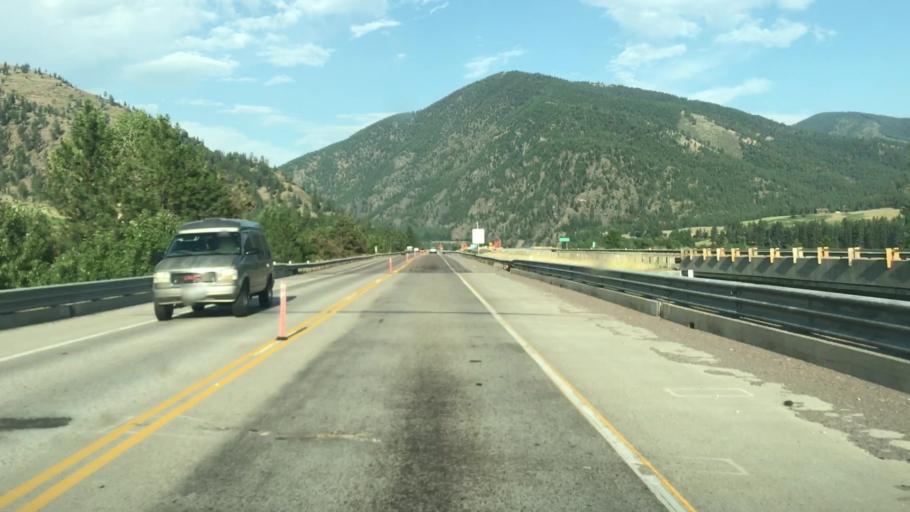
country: US
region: Montana
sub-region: Missoula County
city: Frenchtown
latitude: 47.0043
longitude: -114.5824
